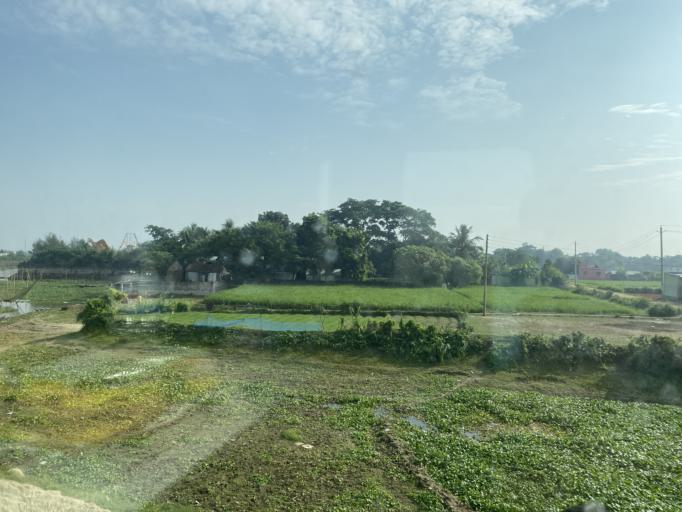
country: BD
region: Chittagong
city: Nabinagar
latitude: 23.9558
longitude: 91.1197
